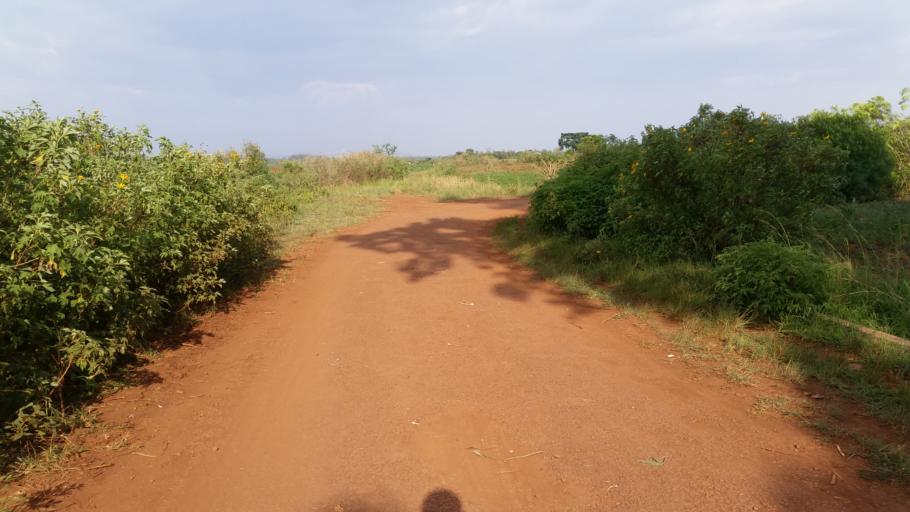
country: UG
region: Eastern Region
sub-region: Busia District
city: Busia
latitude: 0.5470
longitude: 34.0253
